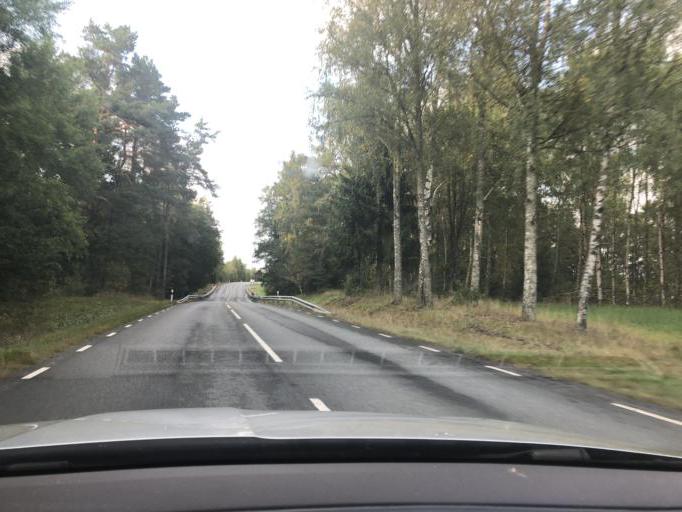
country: SE
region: Joenkoeping
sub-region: Varnamo Kommun
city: Varnamo
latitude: 57.2657
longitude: 14.0545
